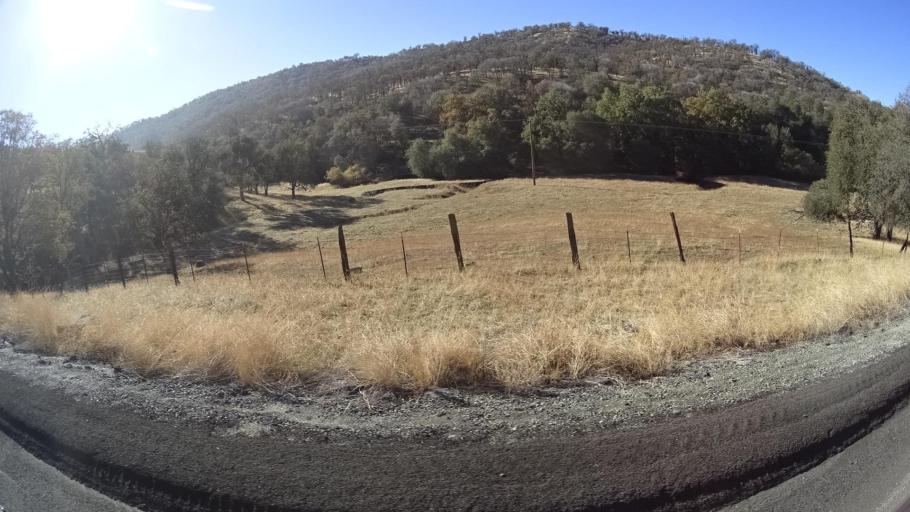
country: US
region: California
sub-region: Kern County
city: Alta Sierra
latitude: 35.7121
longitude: -118.7787
